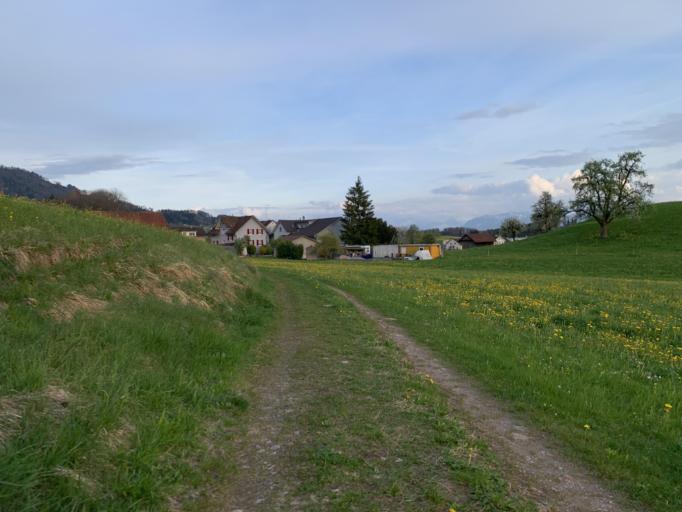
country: CH
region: Zurich
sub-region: Bezirk Hinwil
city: Hinwil
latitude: 47.2902
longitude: 8.8365
